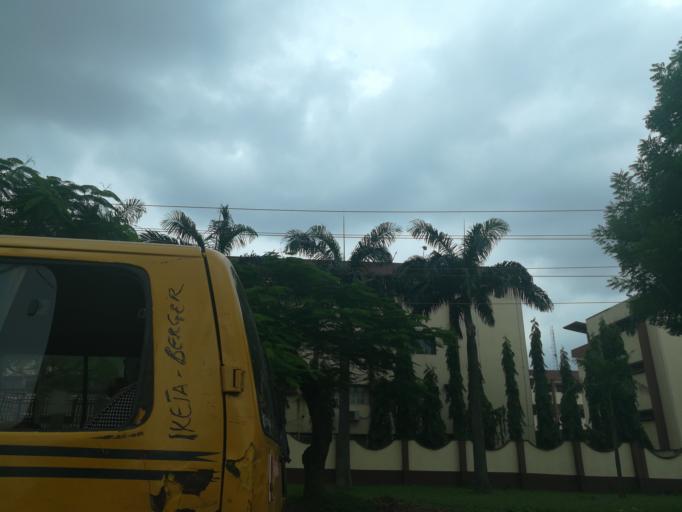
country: NG
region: Lagos
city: Ikeja
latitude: 6.6168
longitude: 3.3591
